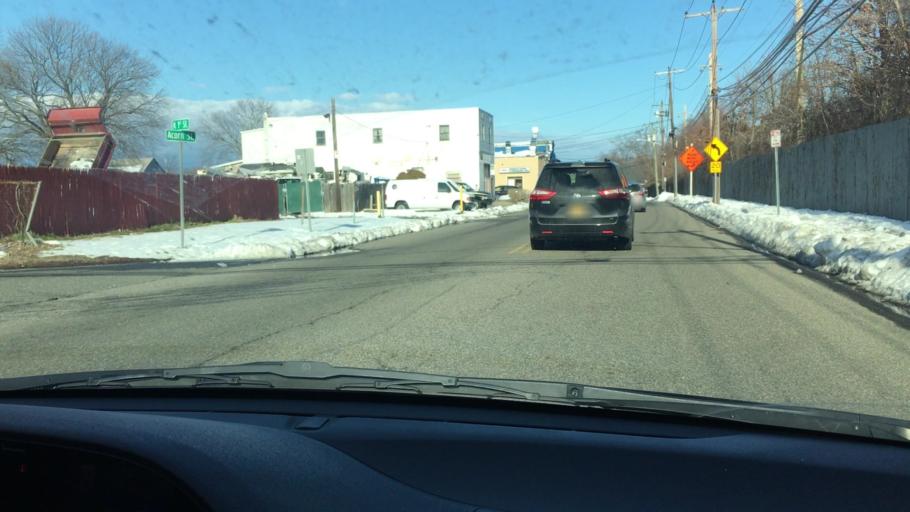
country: US
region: New York
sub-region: Suffolk County
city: Deer Park
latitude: 40.7610
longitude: -73.3316
